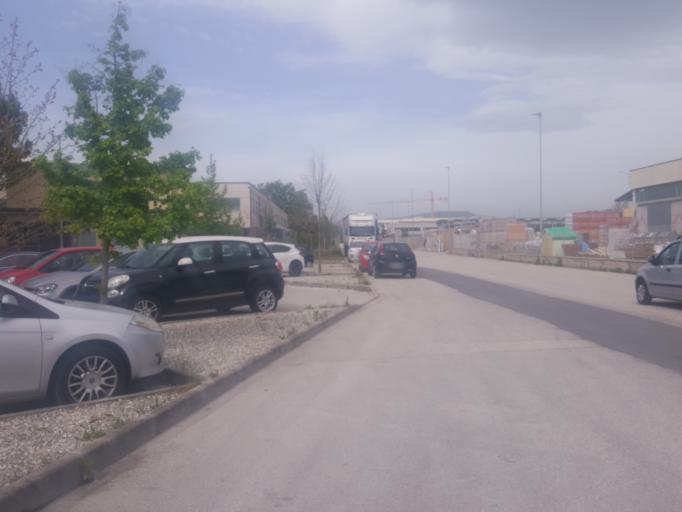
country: IT
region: The Marches
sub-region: Provincia di Ancona
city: Stazione
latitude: 43.5052
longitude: 13.1690
